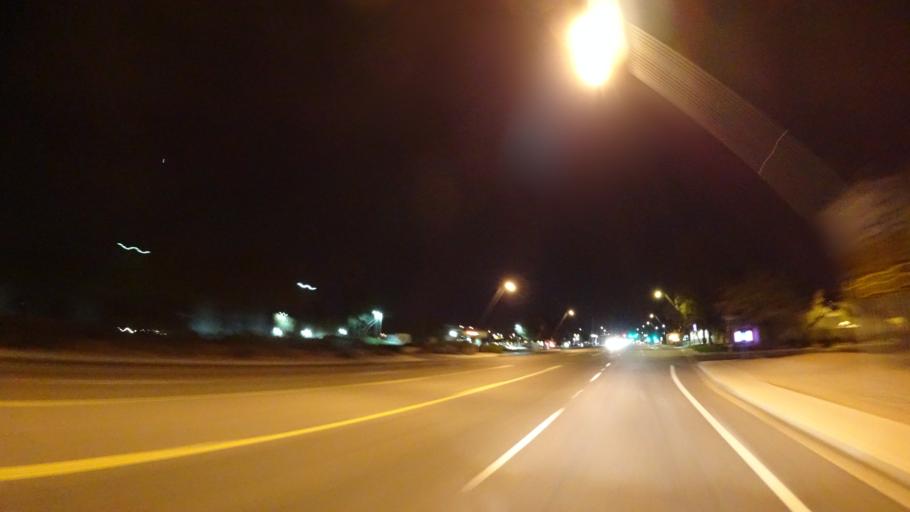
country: US
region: Arizona
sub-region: Maricopa County
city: San Carlos
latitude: 33.3350
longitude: -111.8621
